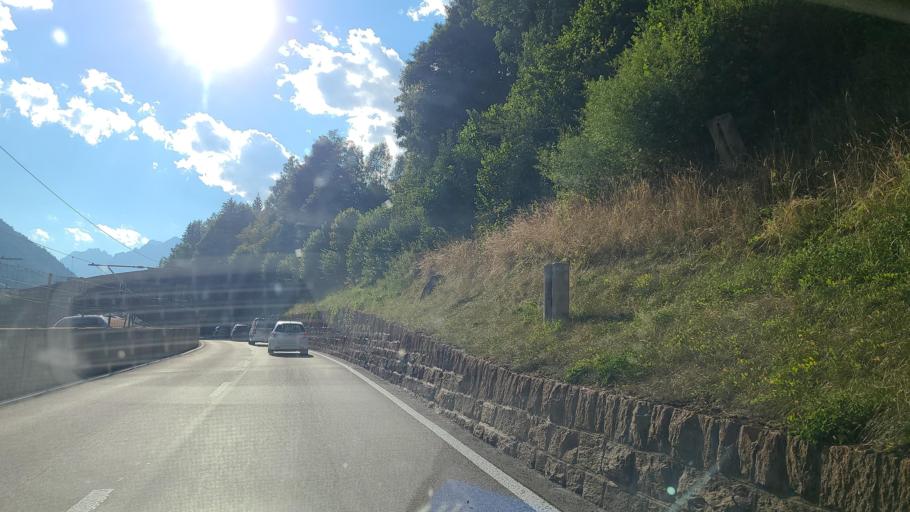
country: CH
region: Ticino
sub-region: Leventina District
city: Airolo
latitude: 46.5273
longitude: 8.6214
